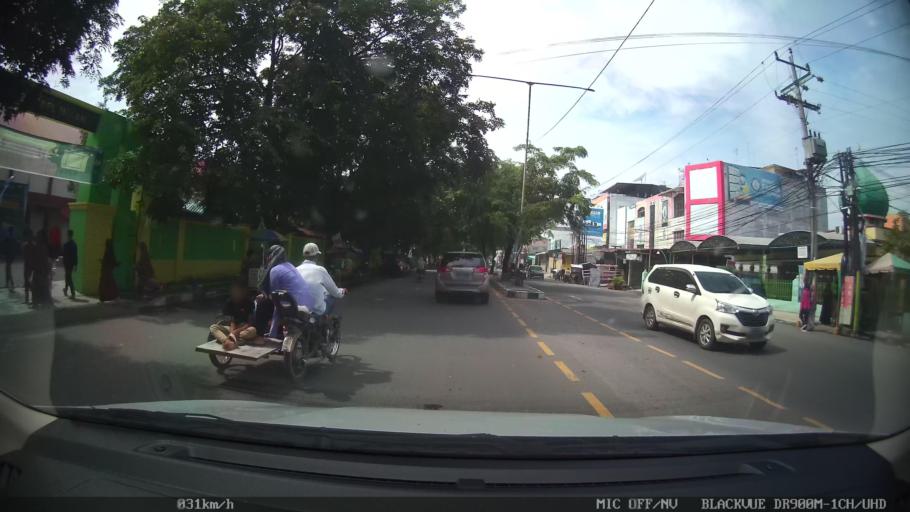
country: ID
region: North Sumatra
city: Medan
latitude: 3.6017
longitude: 98.7067
